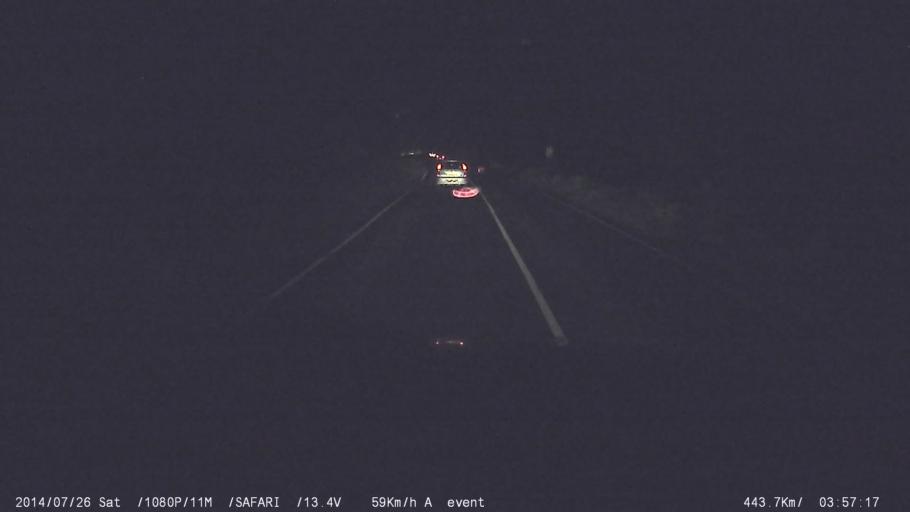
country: IN
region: Kerala
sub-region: Thrissur District
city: Trichur
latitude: 10.5578
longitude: 76.3355
